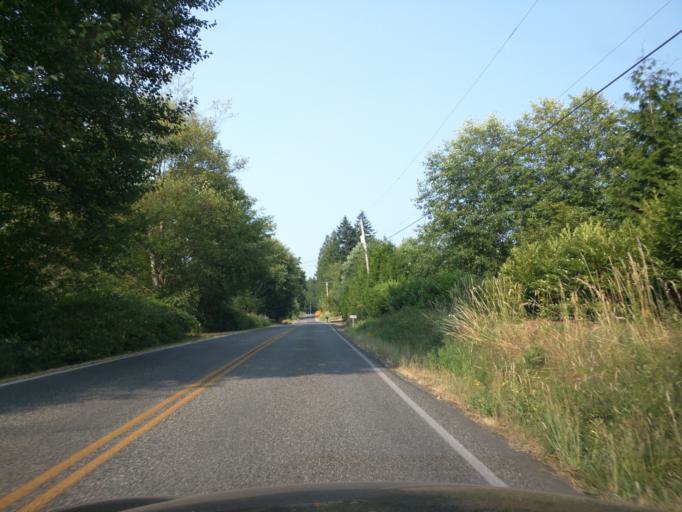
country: US
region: Washington
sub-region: Whatcom County
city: Nooksack
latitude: 48.9295
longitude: -122.2635
